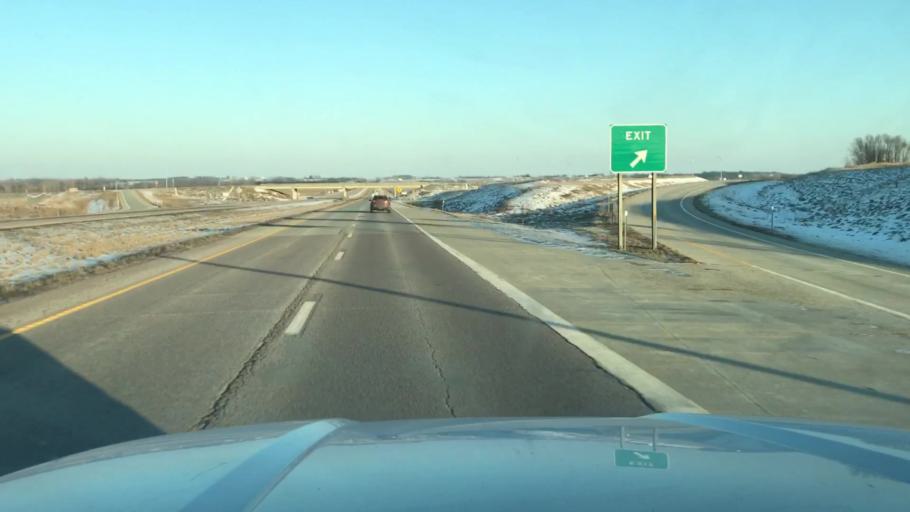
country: US
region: Missouri
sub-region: Buchanan County
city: Saint Joseph
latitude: 39.7480
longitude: -94.7548
